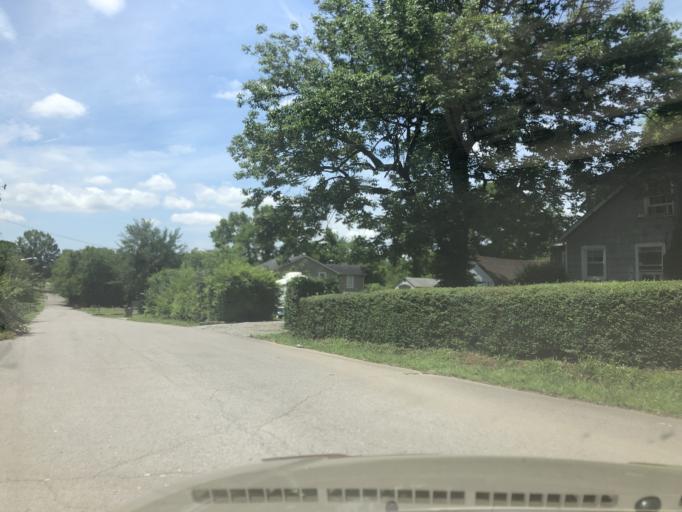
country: US
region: Tennessee
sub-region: Davidson County
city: Lakewood
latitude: 36.2541
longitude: -86.6883
